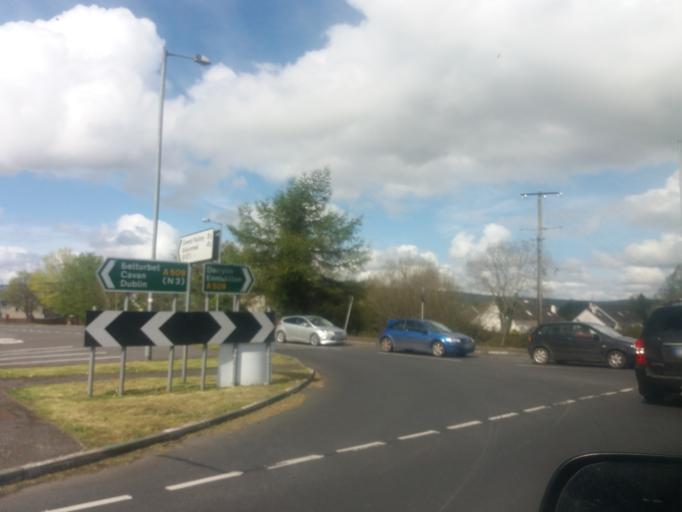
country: IE
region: Ulster
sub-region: An Cabhan
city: Ballyconnell
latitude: 54.1541
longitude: -7.5266
